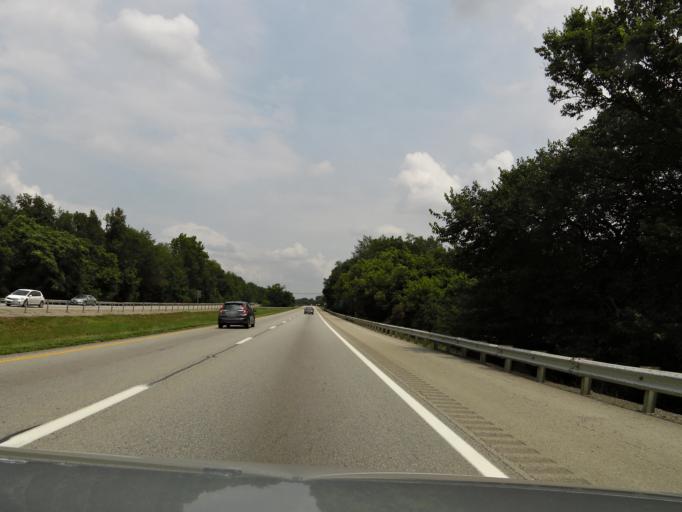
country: US
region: Kentucky
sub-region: Jefferson County
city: Worthington
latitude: 38.3179
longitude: -85.5723
